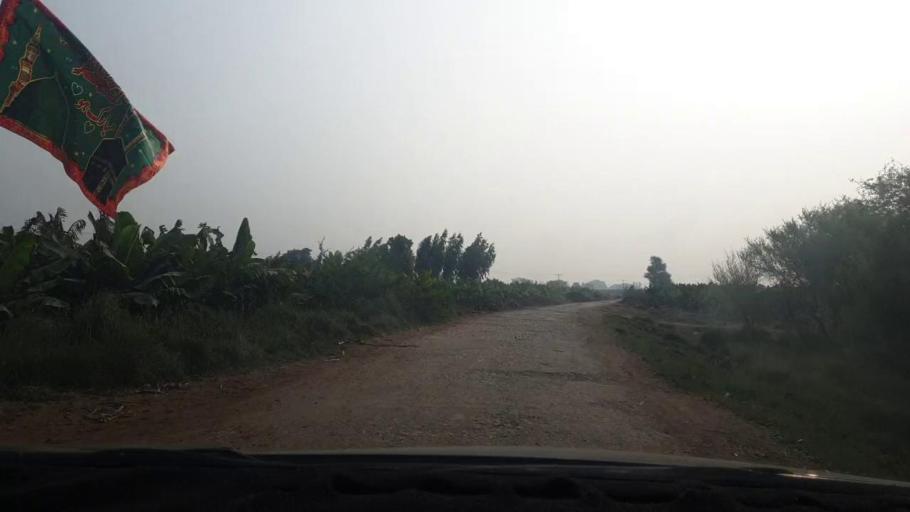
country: PK
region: Sindh
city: Matiari
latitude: 25.5938
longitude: 68.5407
